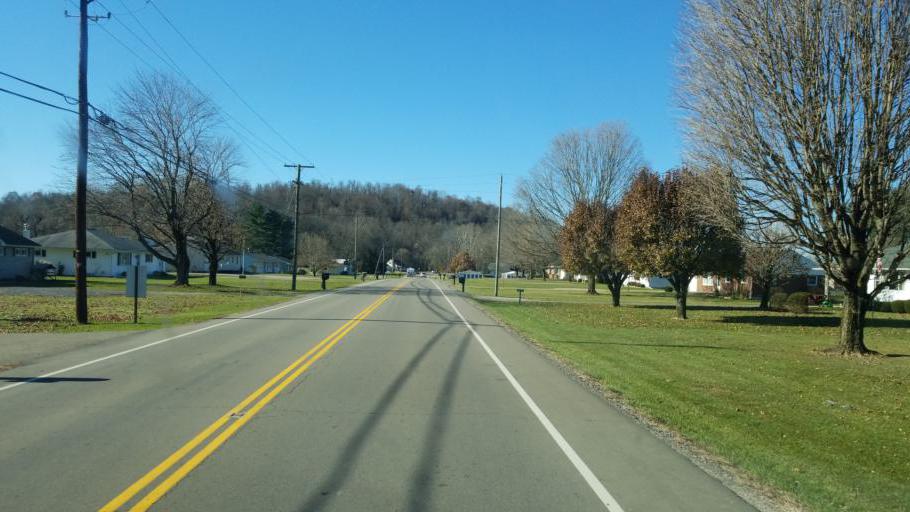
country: US
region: Ohio
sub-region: Coshocton County
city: Coshocton
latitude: 40.3030
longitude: -81.9131
